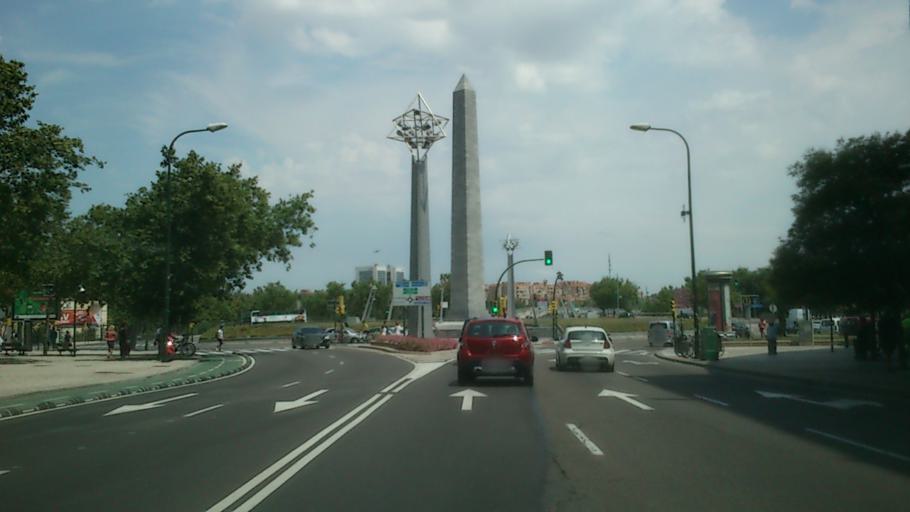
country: ES
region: Aragon
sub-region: Provincia de Zaragoza
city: Almozara
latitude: 41.6581
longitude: -0.8929
